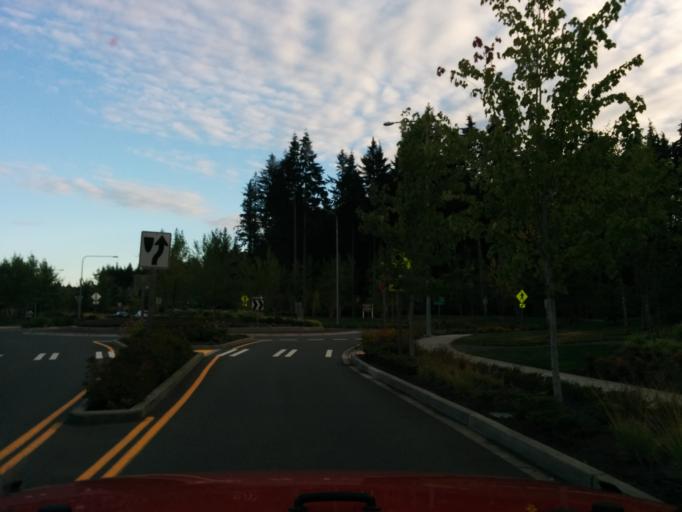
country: US
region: Washington
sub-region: King County
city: Union Hill-Novelty Hill
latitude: 47.6918
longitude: -122.0170
